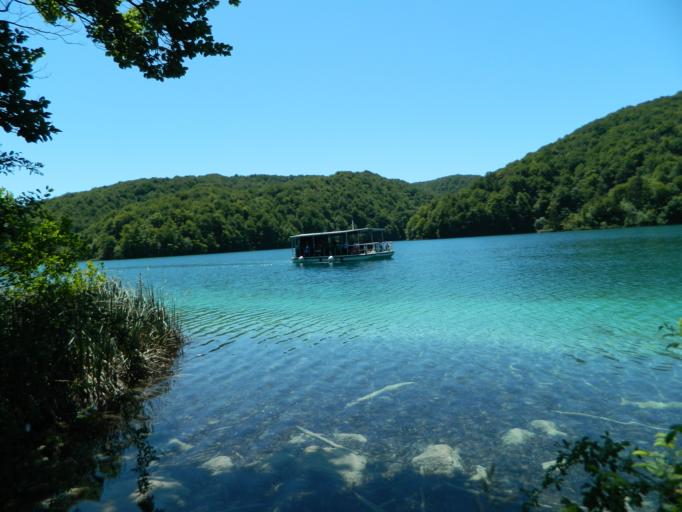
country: HR
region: Licko-Senjska
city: Jezerce
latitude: 44.8901
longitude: 15.6067
